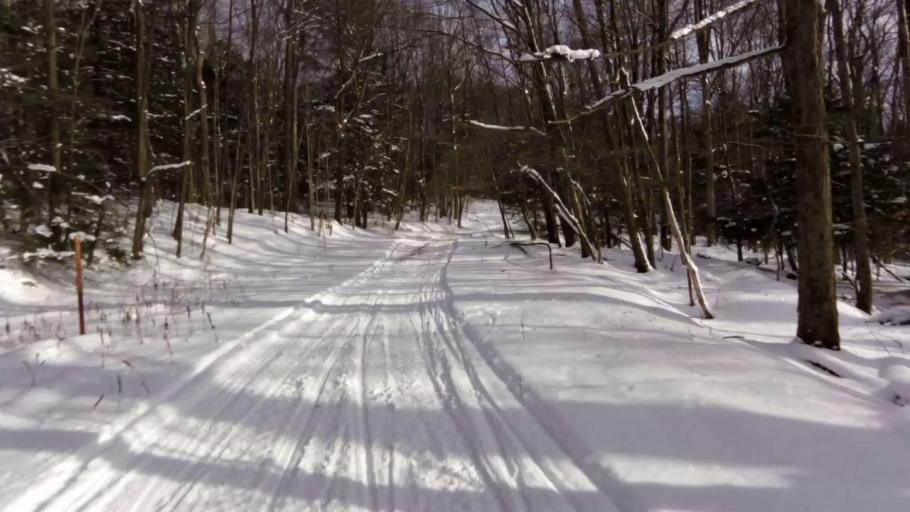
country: US
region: Pennsylvania
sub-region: McKean County
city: Foster Brook
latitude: 41.9995
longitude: -78.5336
